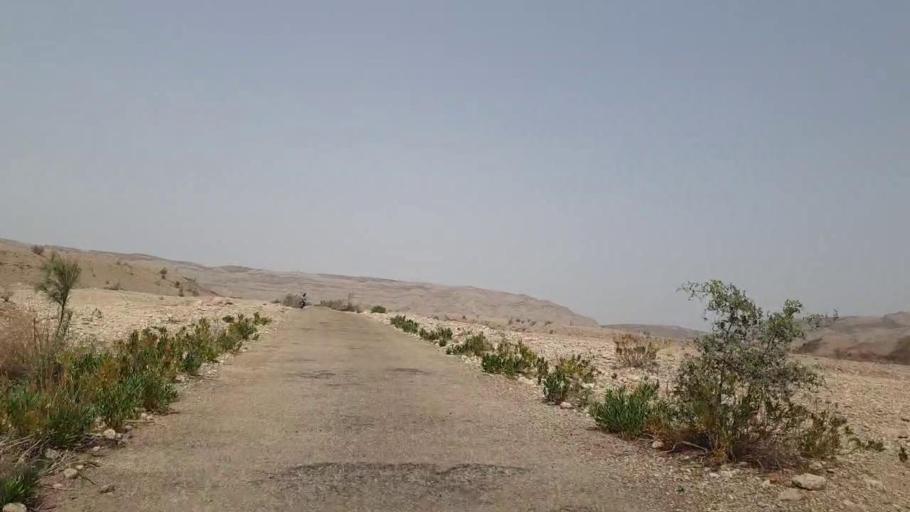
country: PK
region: Sindh
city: Sann
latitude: 25.8875
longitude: 67.9168
